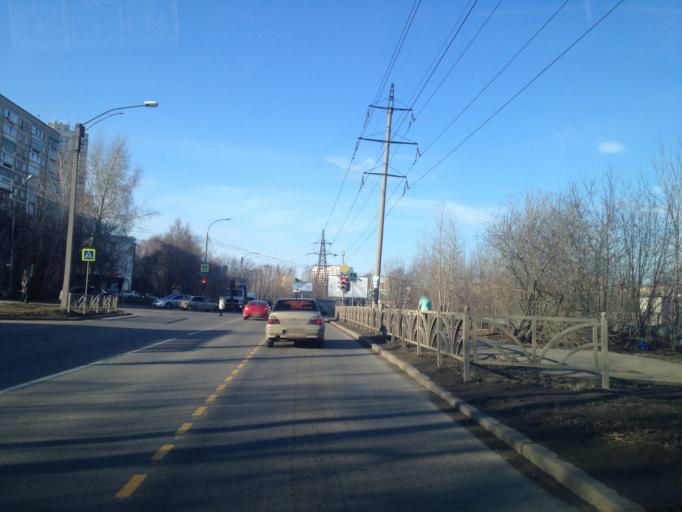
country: RU
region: Sverdlovsk
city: Sovkhoznyy
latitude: 56.7730
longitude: 60.5978
